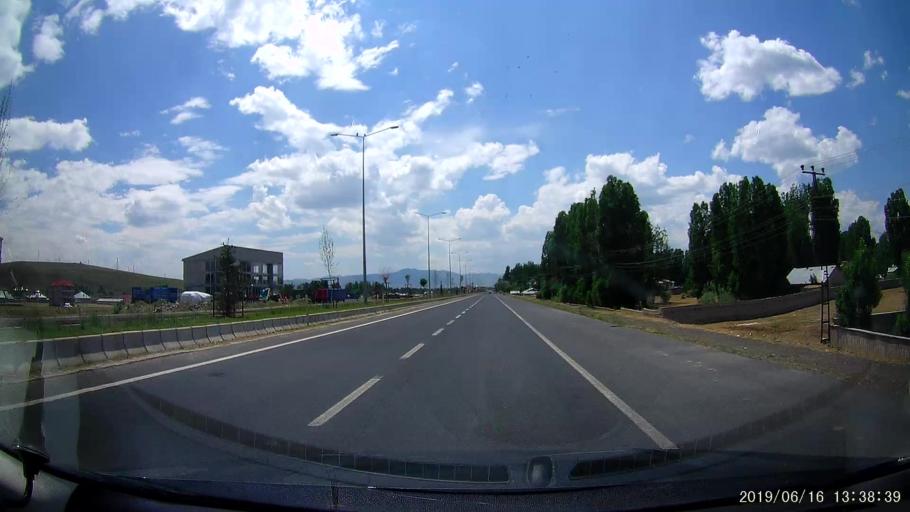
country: TR
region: Agri
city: Agri
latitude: 39.7108
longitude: 43.0710
